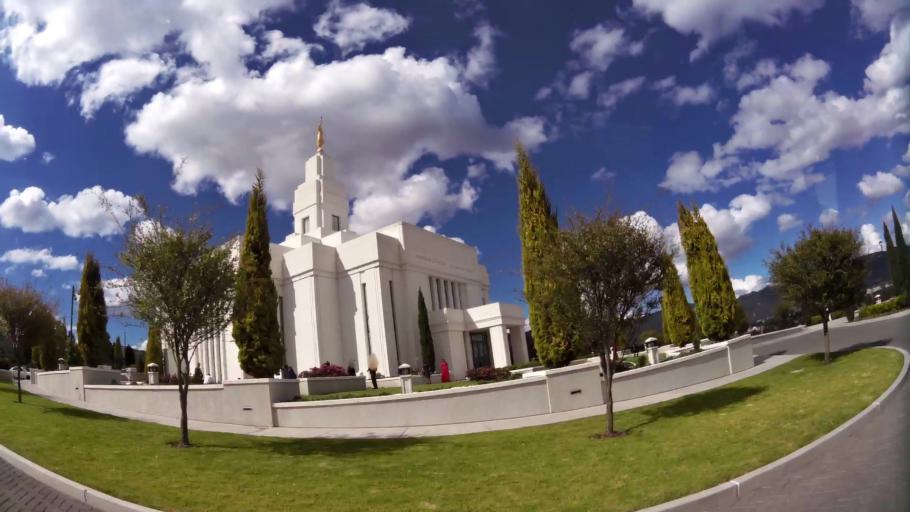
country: GT
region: Quetzaltenango
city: Quetzaltenango
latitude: 14.8462
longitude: -91.5422
